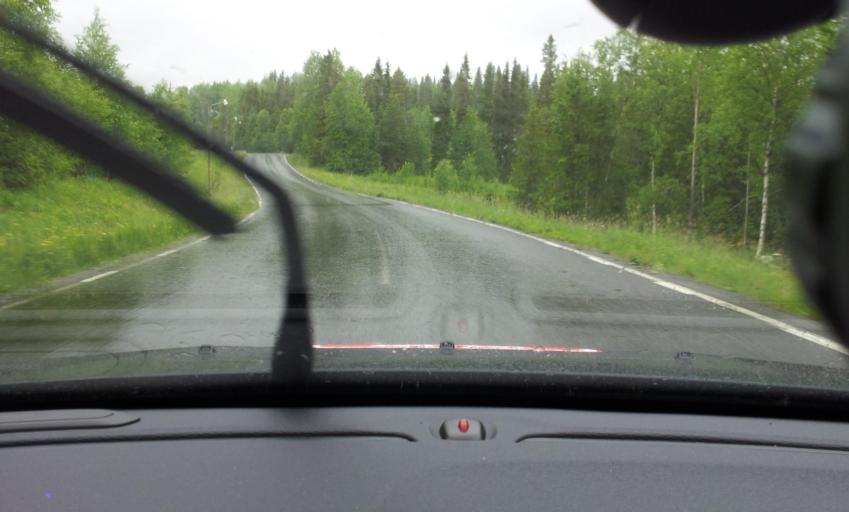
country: SE
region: Jaemtland
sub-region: Are Kommun
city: Are
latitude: 63.3110
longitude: 13.2211
